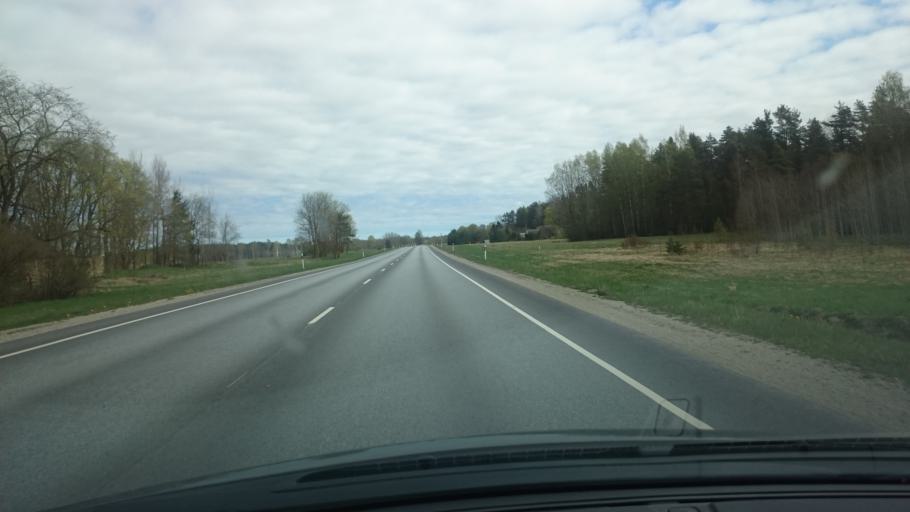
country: EE
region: Laeaene-Virumaa
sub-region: Viru-Nigula vald
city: Kunda
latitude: 59.4087
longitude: 26.6407
